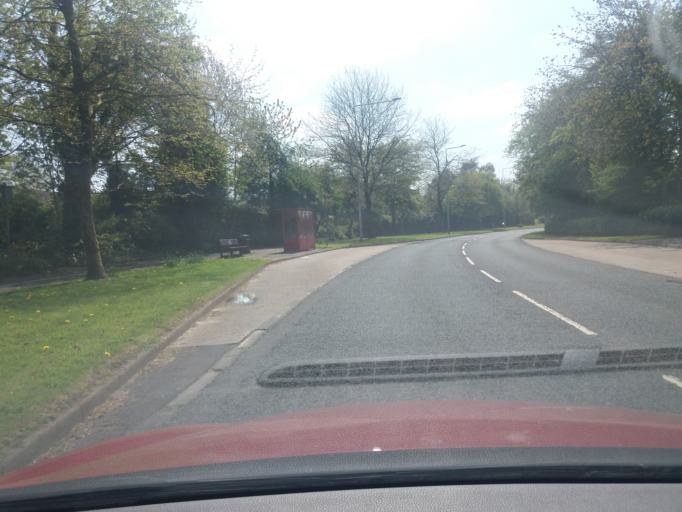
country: GB
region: England
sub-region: Lancashire
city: Chorley
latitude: 53.6650
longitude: -2.6412
